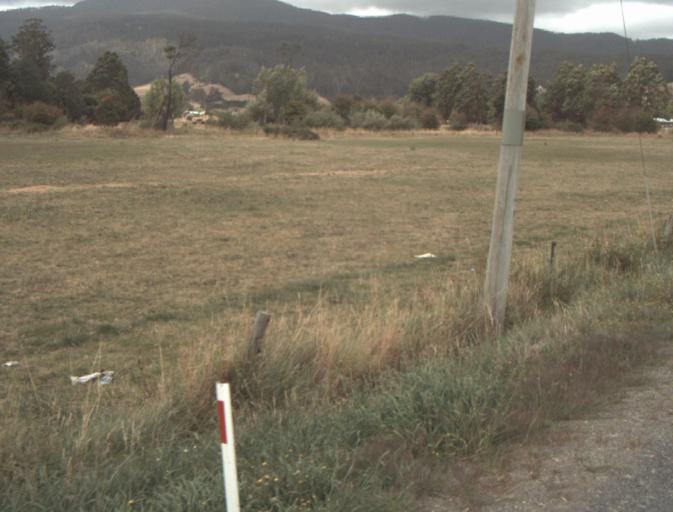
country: AU
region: Tasmania
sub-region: Launceston
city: Mayfield
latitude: -41.2461
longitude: 147.2174
